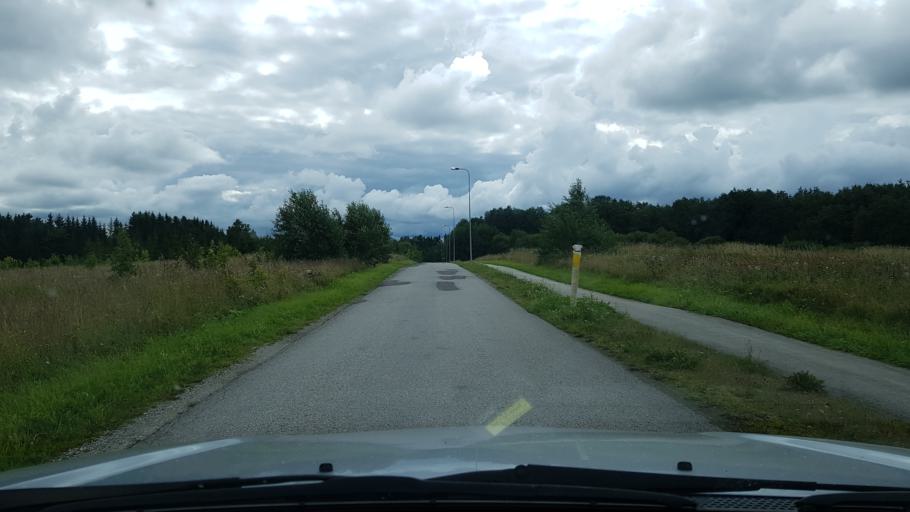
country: EE
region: Harju
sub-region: Rae vald
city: Vaida
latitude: 59.3161
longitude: 24.9479
